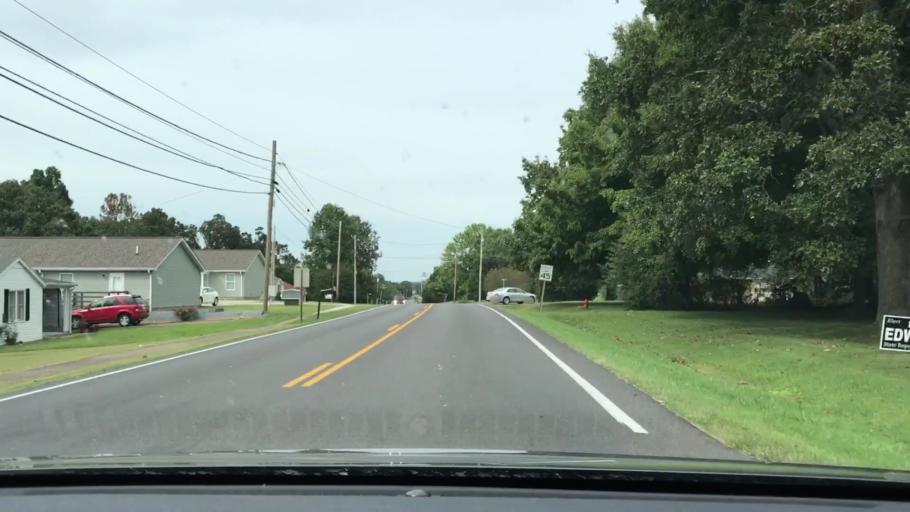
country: US
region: Kentucky
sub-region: Marshall County
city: Benton
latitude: 36.8462
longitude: -88.3498
